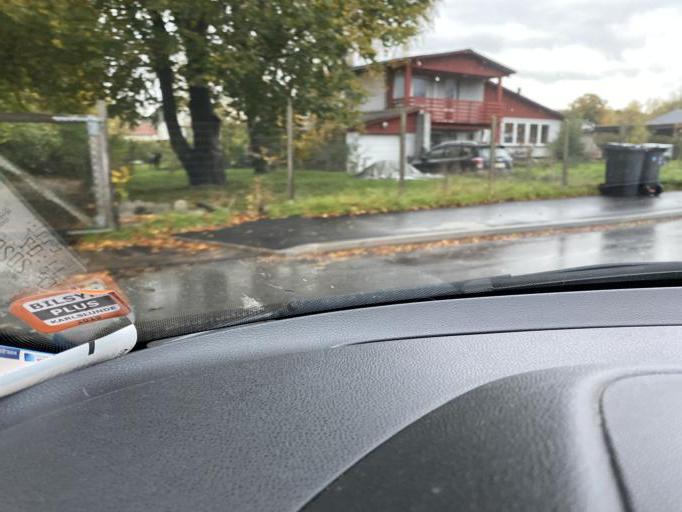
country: DK
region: Zealand
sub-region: Kalundborg Kommune
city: Svebolle
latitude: 55.6522
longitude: 11.2869
